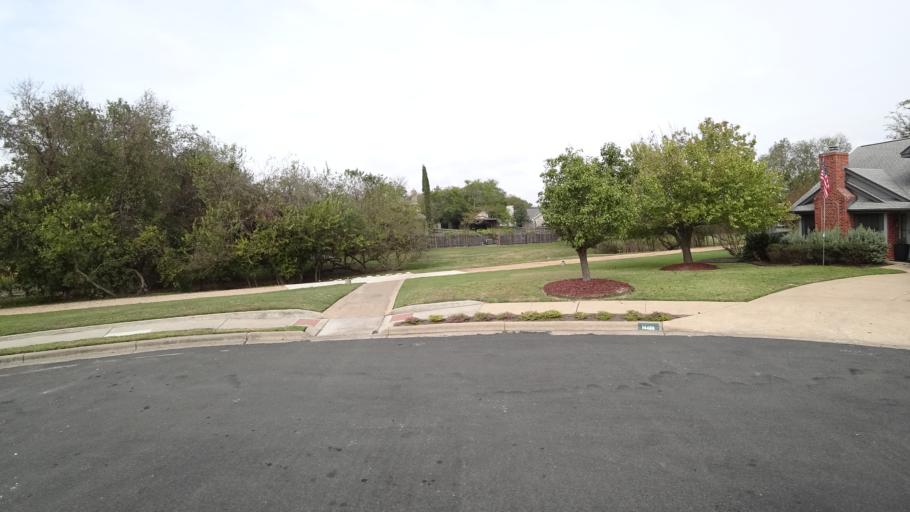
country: US
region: Texas
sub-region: Travis County
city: Wells Branch
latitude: 30.4402
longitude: -97.6797
